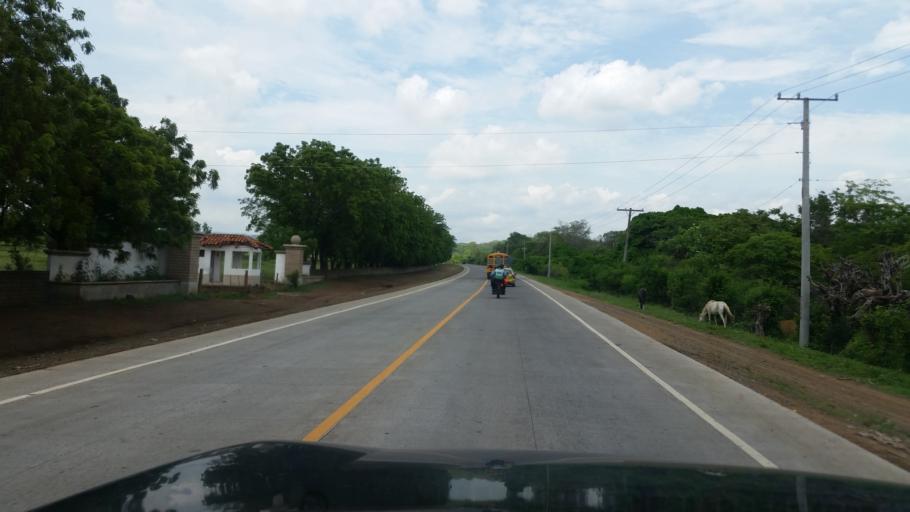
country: NI
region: Managua
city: Carlos Fonseca Amador
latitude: 12.0645
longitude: -86.4716
